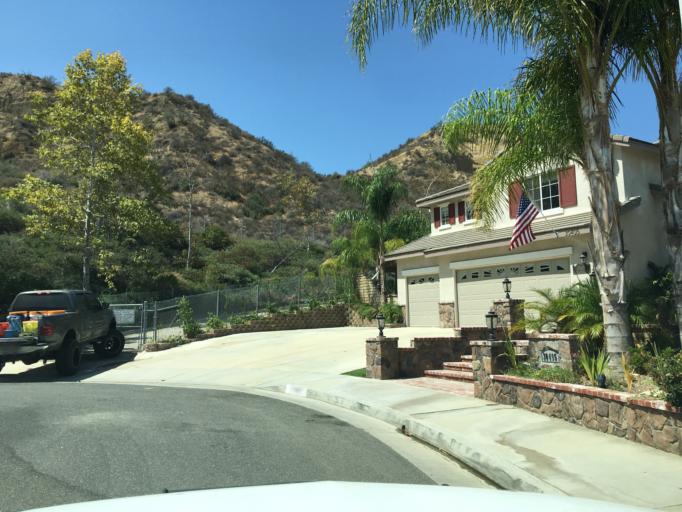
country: US
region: California
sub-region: Los Angeles County
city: Castaic
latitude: 34.4698
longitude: -118.6348
